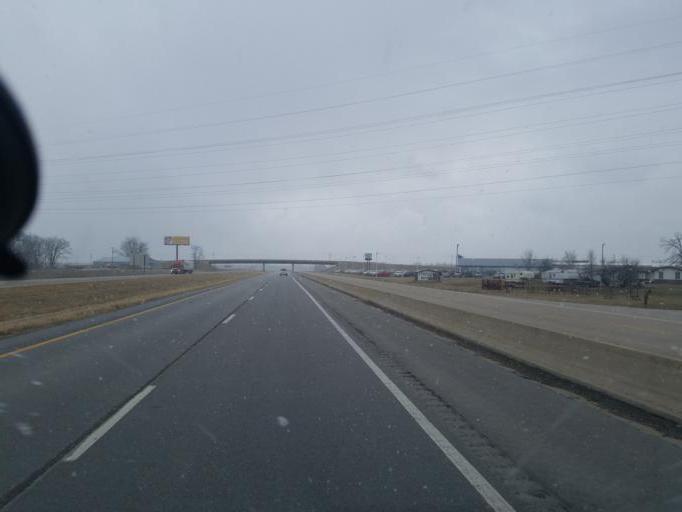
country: US
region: Missouri
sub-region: Randolph County
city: Moberly
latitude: 39.4340
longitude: -92.4178
